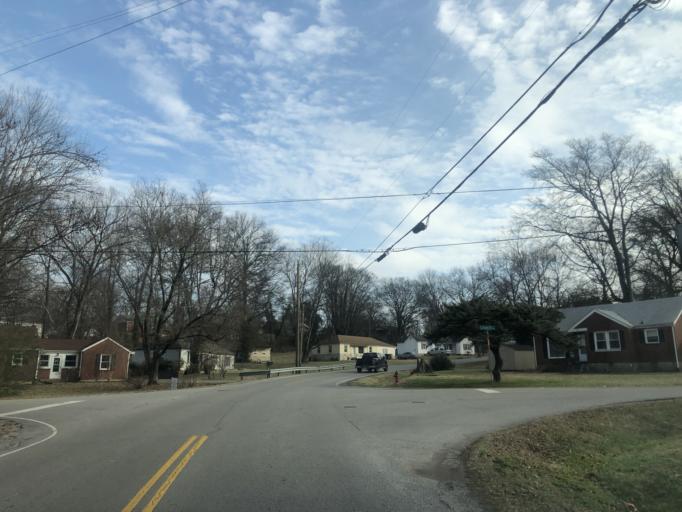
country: US
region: Tennessee
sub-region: Davidson County
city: Oak Hill
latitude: 36.1146
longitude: -86.7182
